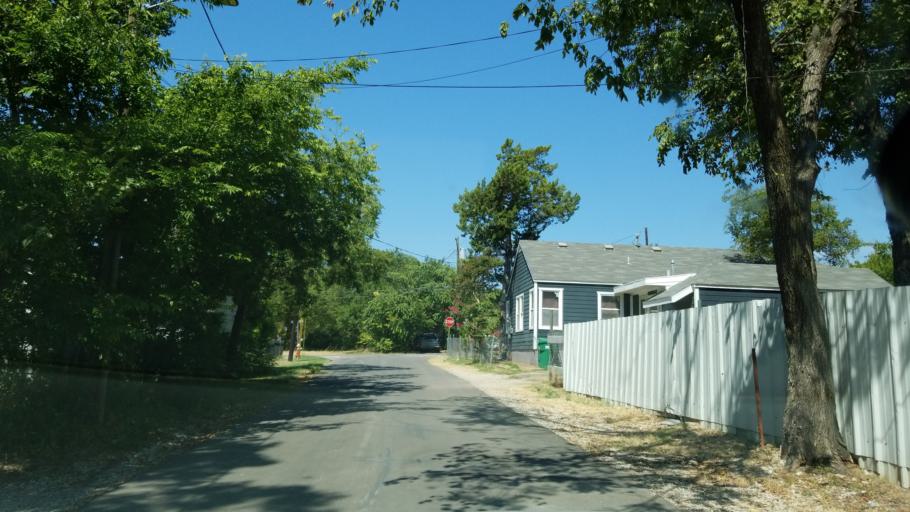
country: US
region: Texas
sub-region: Dallas County
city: Cockrell Hill
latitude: 32.7395
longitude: -96.8866
